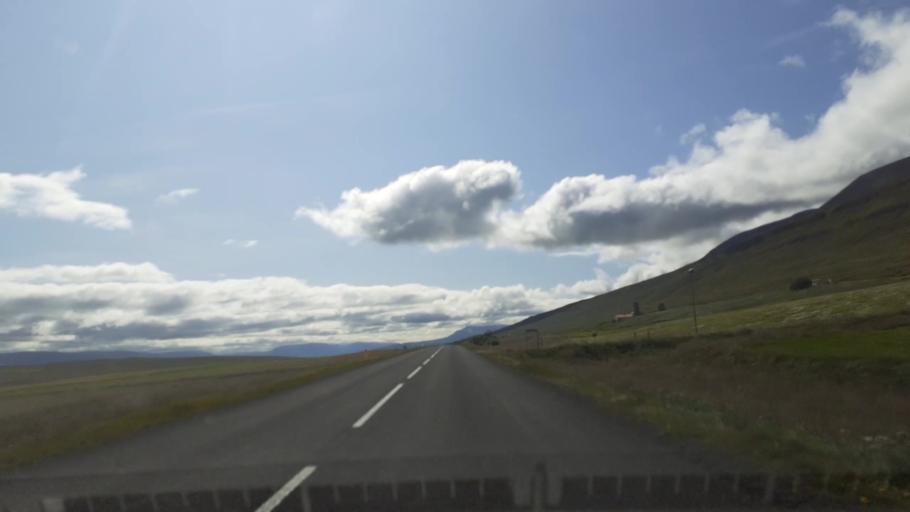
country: IS
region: Northeast
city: Akureyri
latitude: 65.8627
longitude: -18.2609
